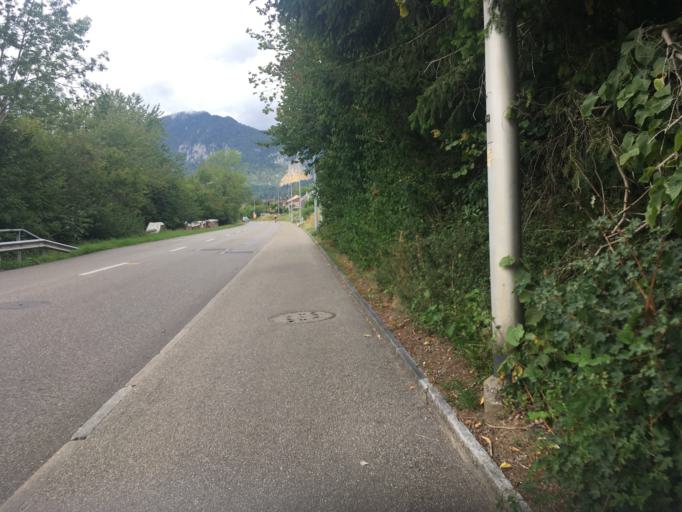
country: CH
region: Solothurn
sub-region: Bezirk Lebern
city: Langendorf
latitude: 47.2254
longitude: 7.5122
